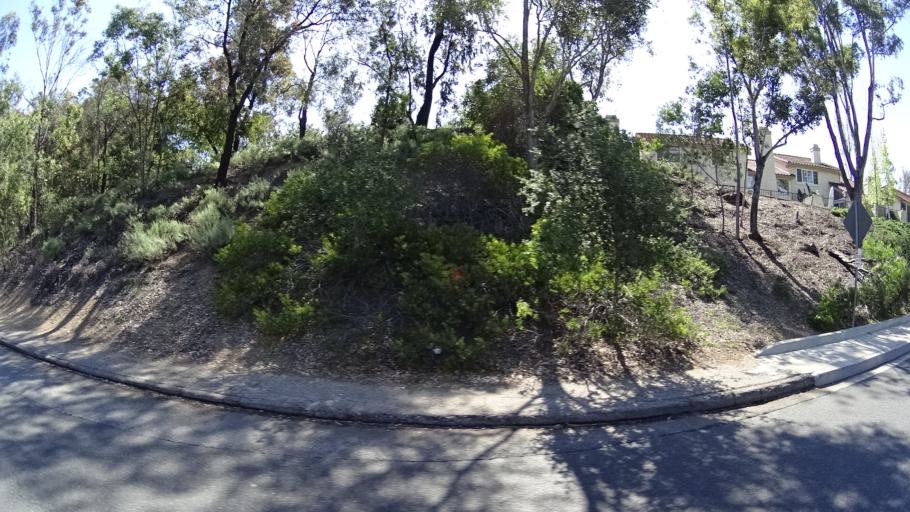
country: US
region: California
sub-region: Ventura County
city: Casa Conejo
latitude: 34.1811
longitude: -118.8925
